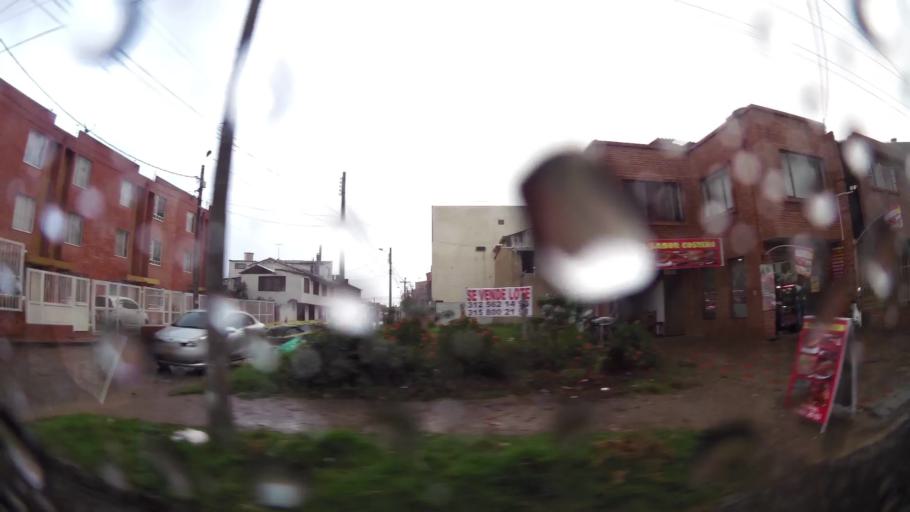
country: CO
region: Cundinamarca
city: Chia
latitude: 4.8628
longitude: -74.0649
